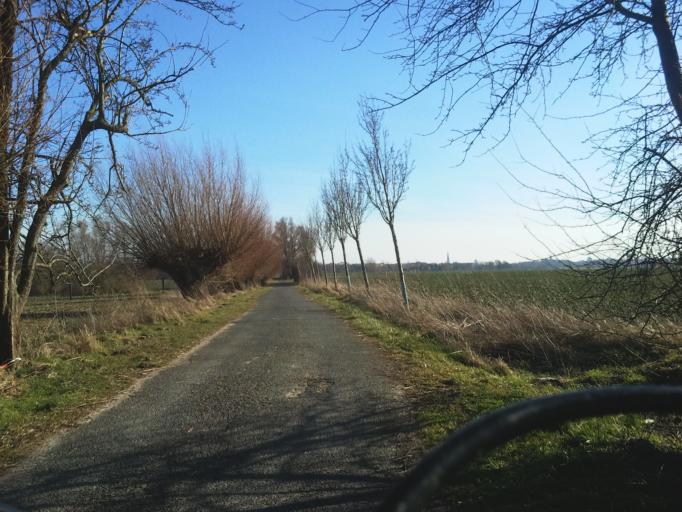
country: DE
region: Mecklenburg-Vorpommern
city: Dierkow-West
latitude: 54.1291
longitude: 12.1263
